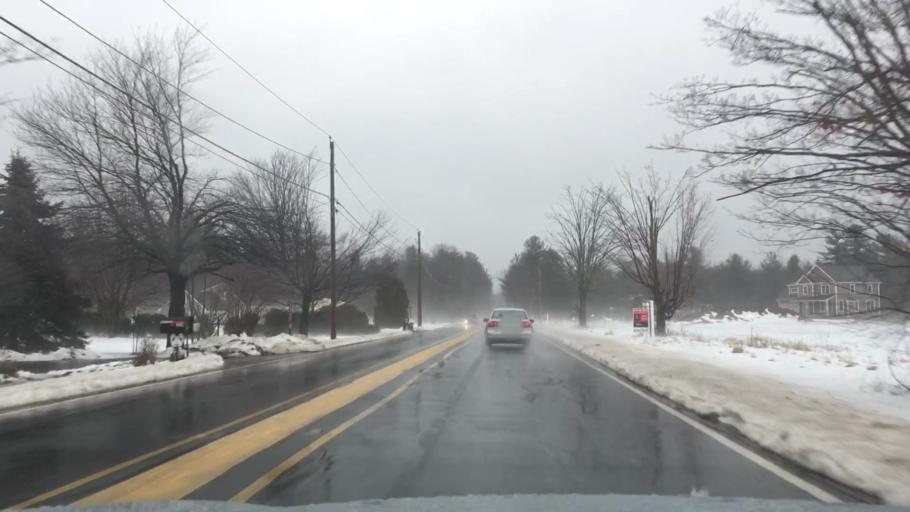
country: US
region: Massachusetts
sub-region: Hampshire County
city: Granby
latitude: 42.2288
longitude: -72.4882
